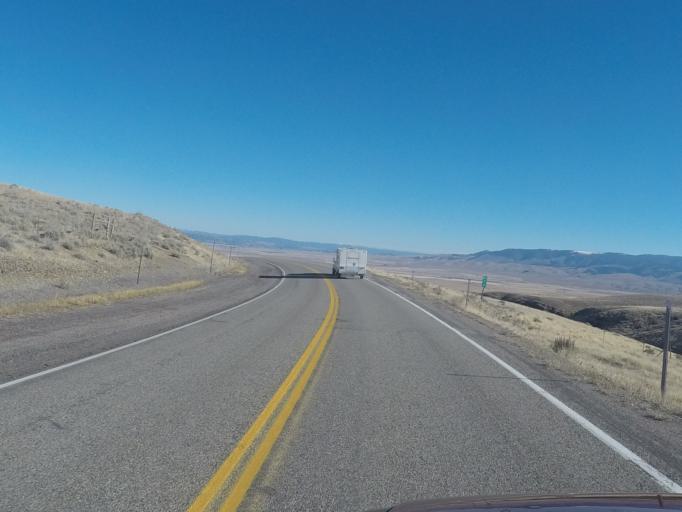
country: US
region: Montana
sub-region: Meagher County
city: White Sulphur Springs
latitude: 46.3796
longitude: -110.9891
